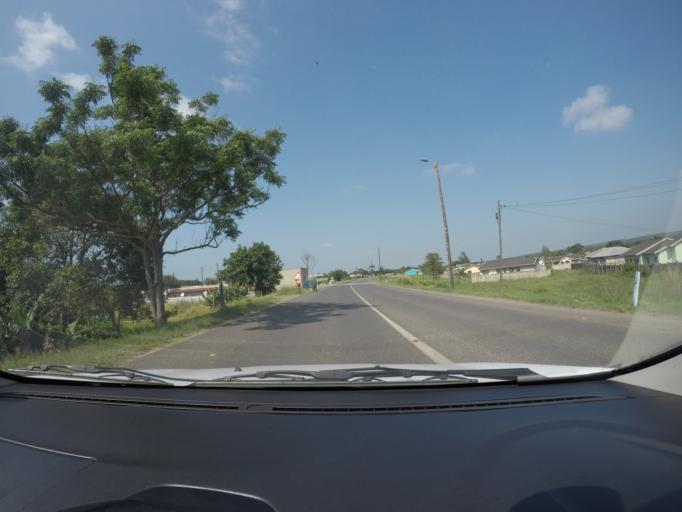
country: ZA
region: KwaZulu-Natal
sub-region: uThungulu District Municipality
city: eSikhawini
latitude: -28.8910
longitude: 31.8919
